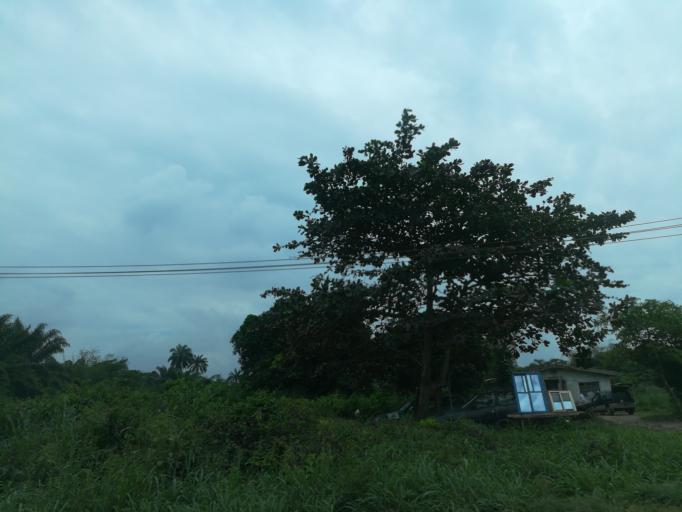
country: NG
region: Lagos
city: Ejirin
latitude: 6.6460
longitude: 3.7724
